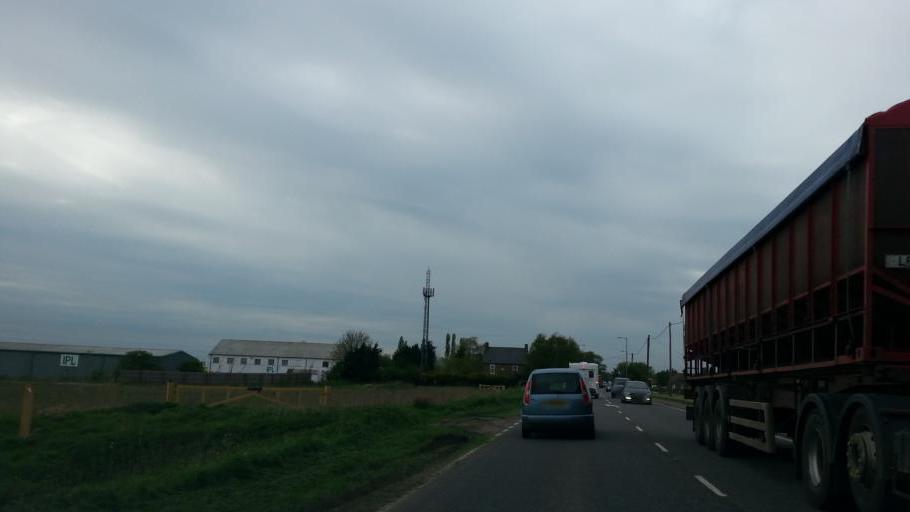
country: GB
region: England
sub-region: Cambridgeshire
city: March
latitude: 52.5663
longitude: 0.0621
